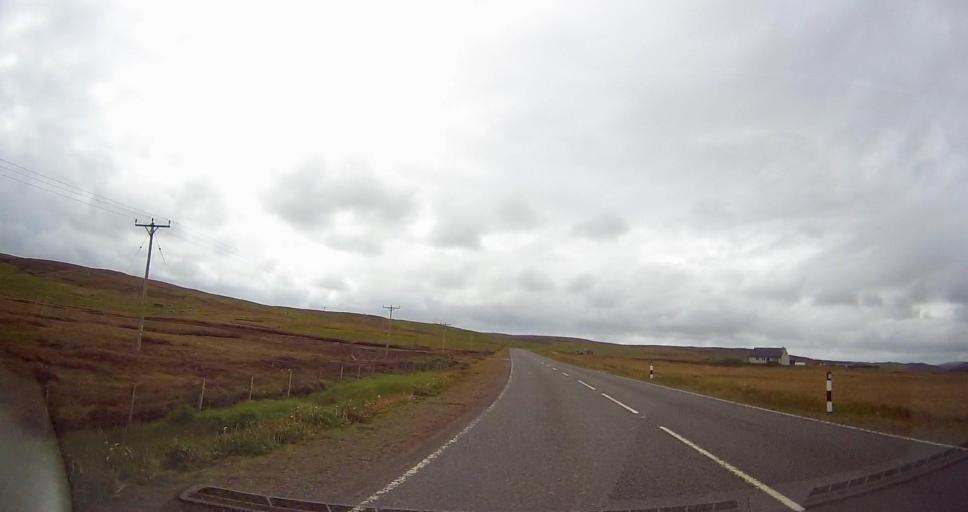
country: GB
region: Scotland
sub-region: Shetland Islands
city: Lerwick
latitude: 60.2571
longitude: -1.4420
